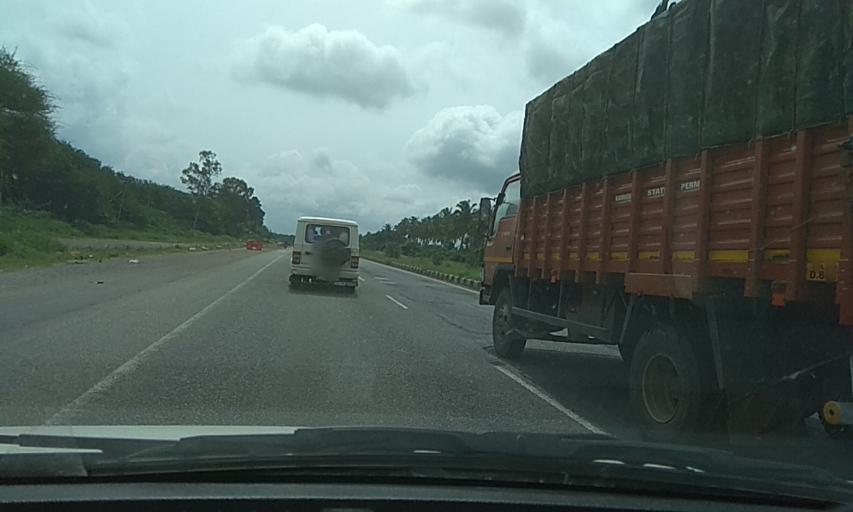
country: IN
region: Karnataka
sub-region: Davanagere
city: Mayakonda
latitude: 14.4018
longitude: 76.0103
